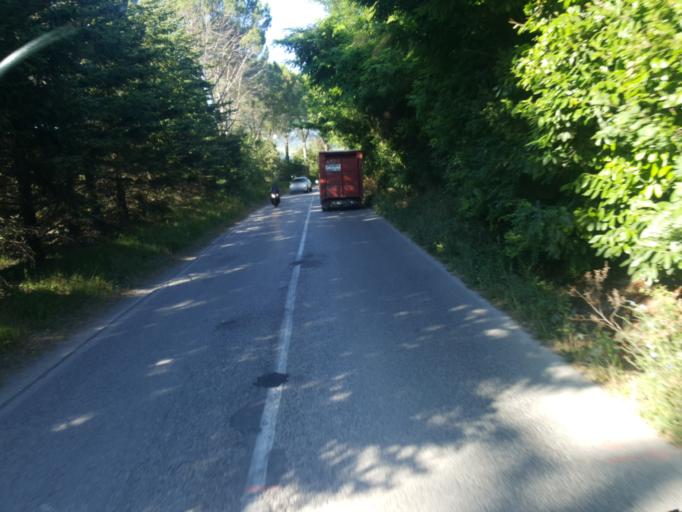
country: IT
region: The Marches
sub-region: Provincia di Pesaro e Urbino
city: Montecalvo in Foglia
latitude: 43.7936
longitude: 12.6497
